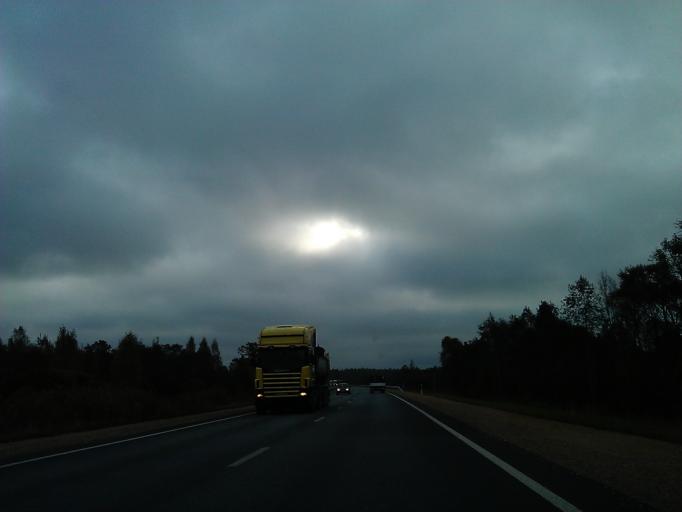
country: LV
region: Aizkraukles Rajons
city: Aizkraukle
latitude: 56.7065
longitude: 25.2364
